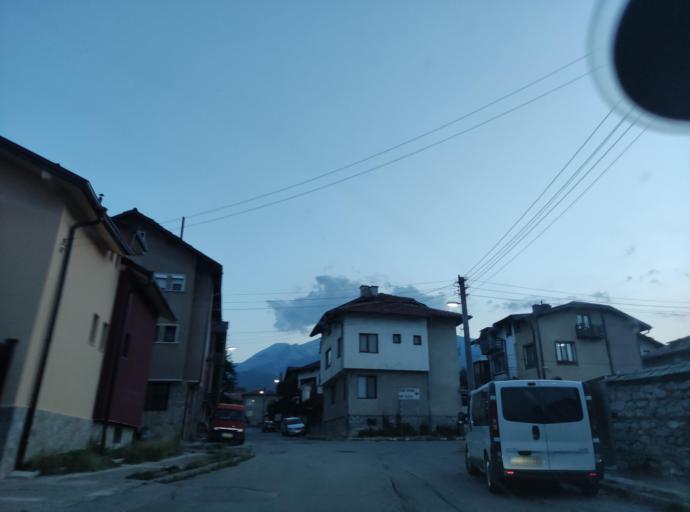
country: BG
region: Blagoevgrad
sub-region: Obshtina Bansko
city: Bansko
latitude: 41.8302
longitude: 23.4870
